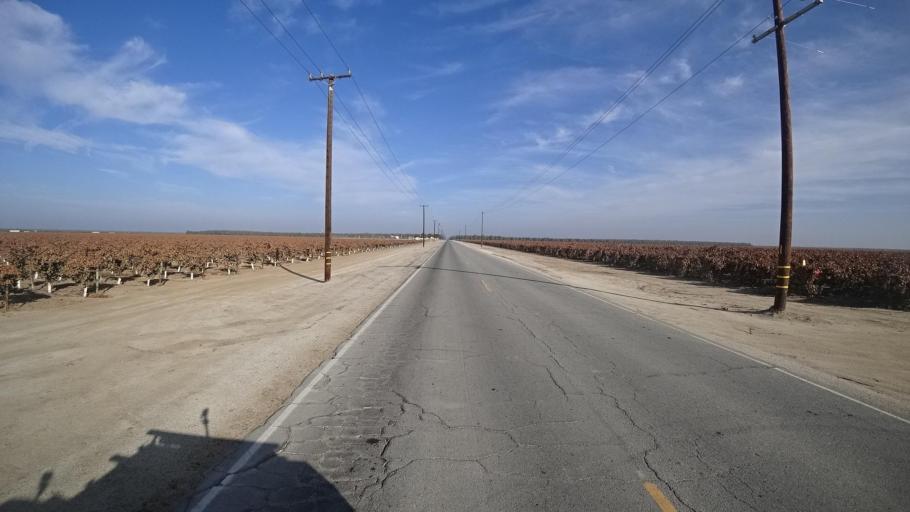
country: US
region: California
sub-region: Kern County
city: McFarland
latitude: 35.6095
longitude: -119.2044
